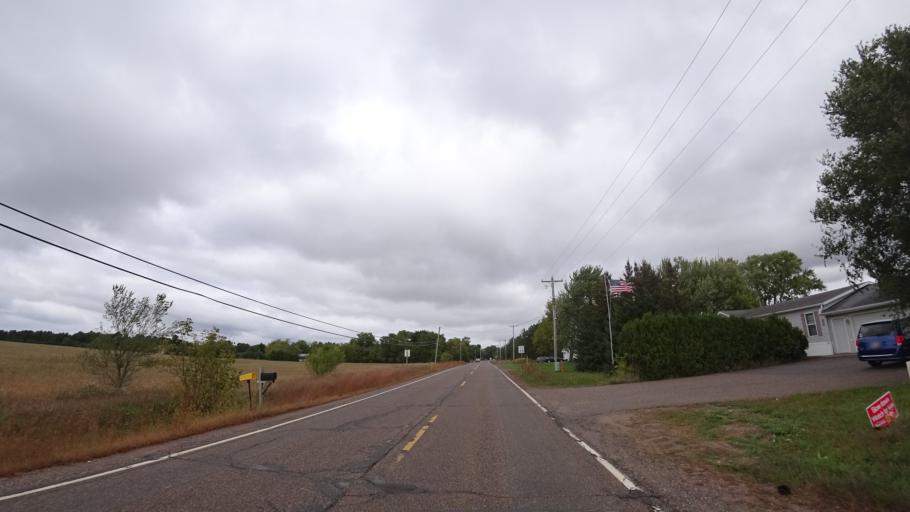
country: US
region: Wisconsin
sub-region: Chippewa County
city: Lake Wissota
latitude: 44.9415
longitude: -91.2679
